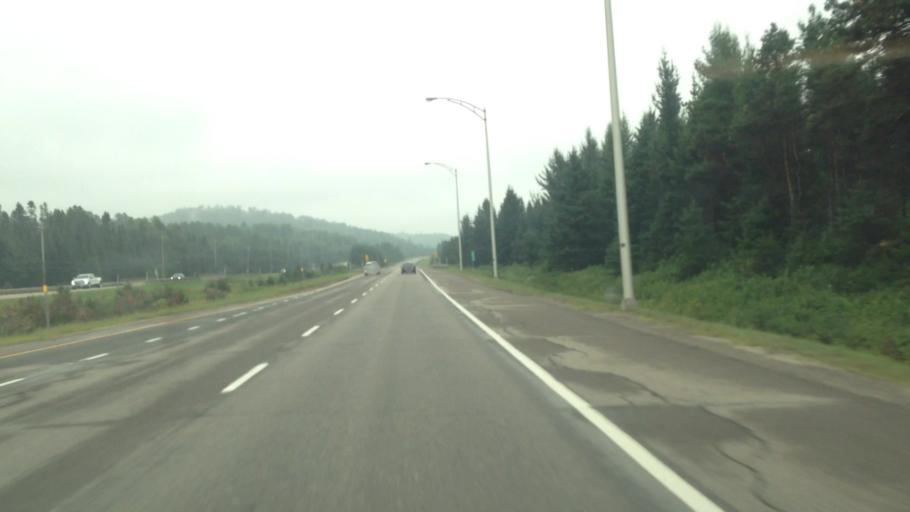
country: CA
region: Quebec
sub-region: Laurentides
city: Sainte-Agathe-des-Monts
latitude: 46.0971
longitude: -74.3553
